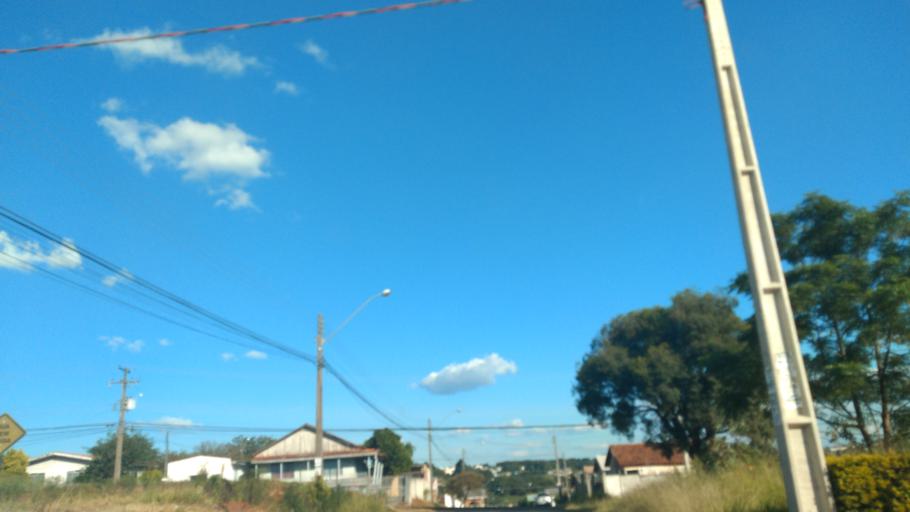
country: BR
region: Parana
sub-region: Guarapuava
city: Guarapuava
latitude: -25.4010
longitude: -51.4802
